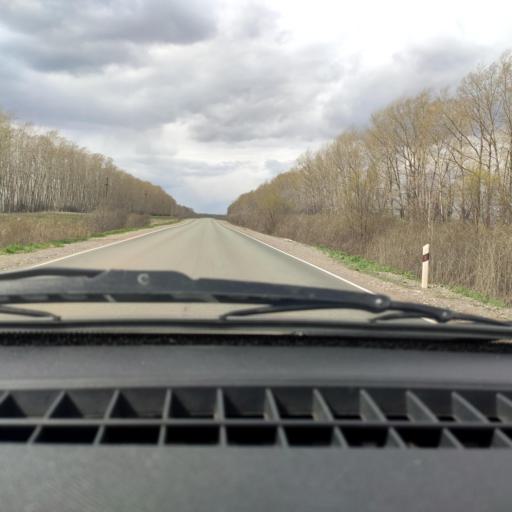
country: RU
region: Bashkortostan
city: Alekseyevka
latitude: 55.0593
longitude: 55.1096
